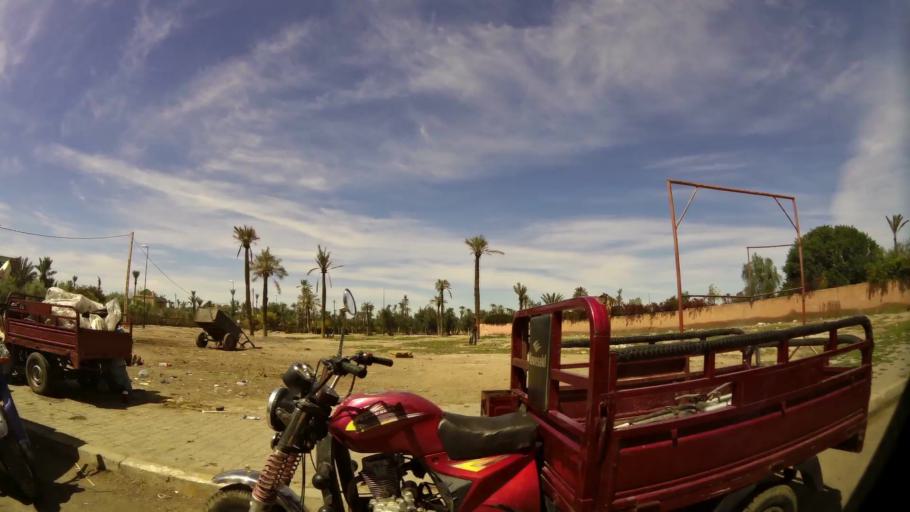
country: MA
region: Marrakech-Tensift-Al Haouz
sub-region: Marrakech
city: Marrakesh
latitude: 31.6656
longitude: -7.9845
